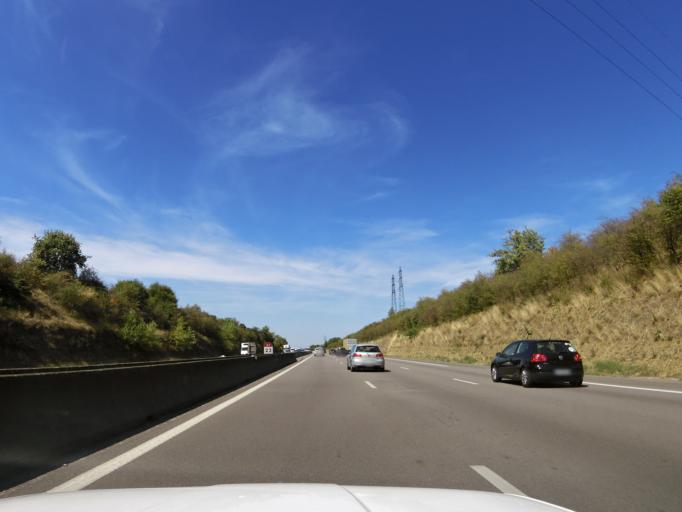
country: FR
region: Rhone-Alpes
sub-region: Departement de l'Isere
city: Chanas
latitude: 45.3292
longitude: 4.8116
